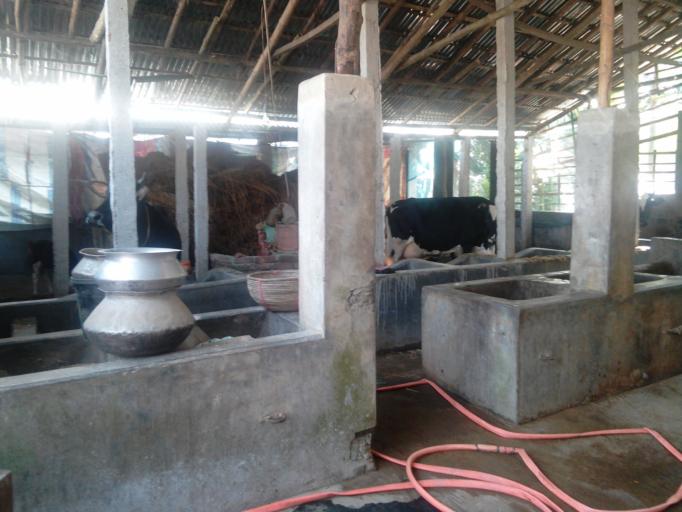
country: BD
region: Khulna
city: Kesabpur
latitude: 22.7829
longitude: 89.2779
